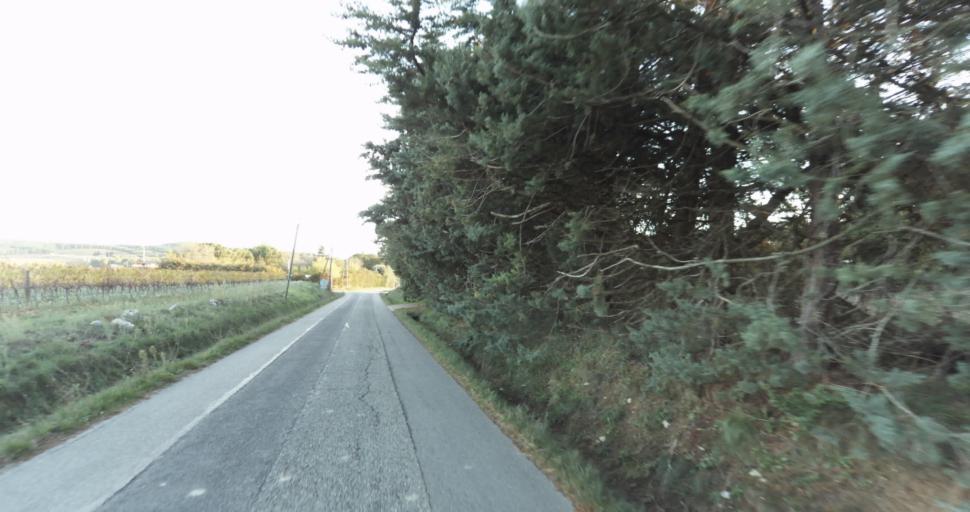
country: FR
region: Provence-Alpes-Cote d'Azur
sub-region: Departement des Bouches-du-Rhone
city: Venelles
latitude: 43.5788
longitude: 5.4970
